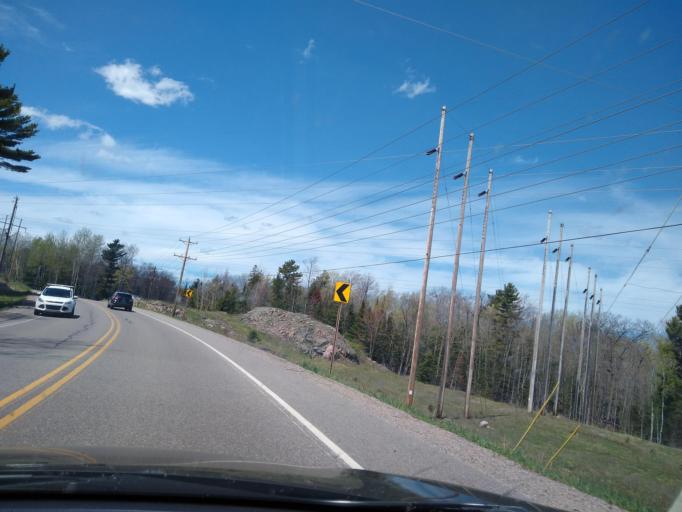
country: US
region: Michigan
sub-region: Marquette County
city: Trowbridge Park
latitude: 46.5780
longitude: -87.4242
